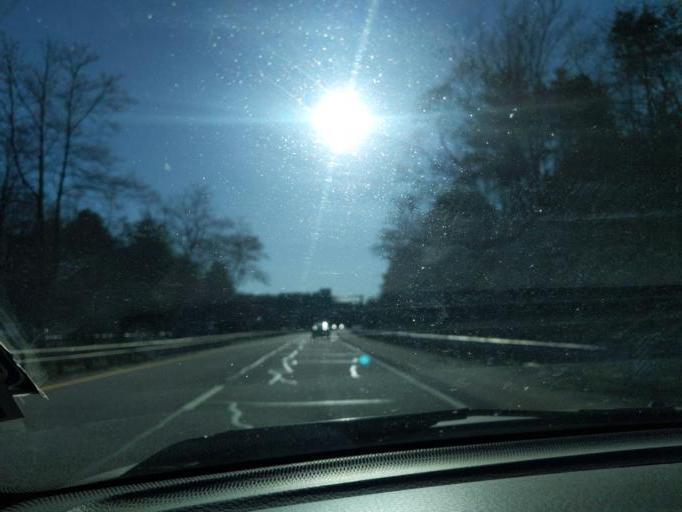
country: US
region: Massachusetts
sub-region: Essex County
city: Essex
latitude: 42.5913
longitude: -70.7791
